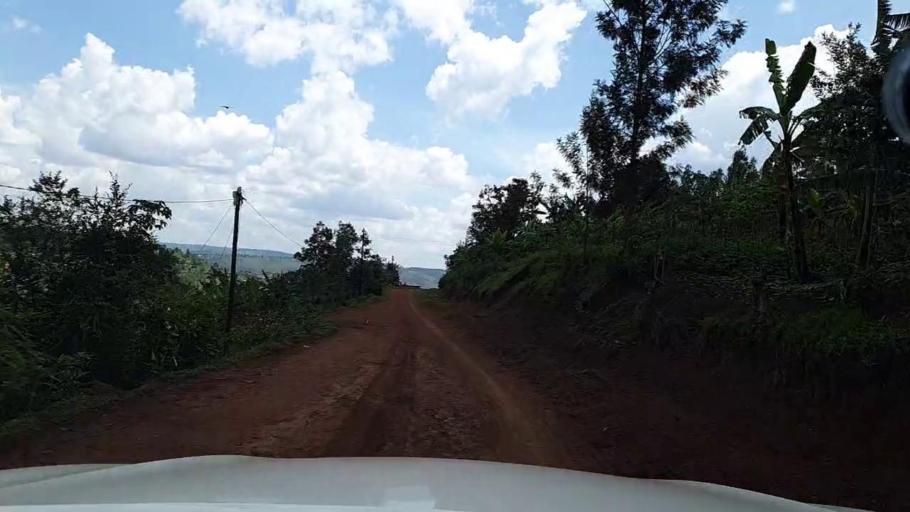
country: RW
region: Southern Province
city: Butare
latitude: -2.7571
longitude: 29.7468
